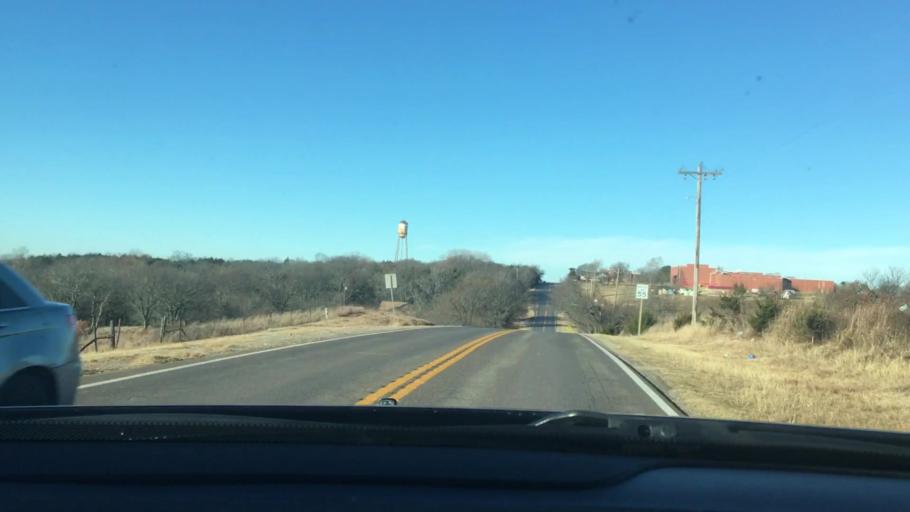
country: US
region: Oklahoma
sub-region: Murray County
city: Sulphur
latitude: 34.5110
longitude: -96.9462
